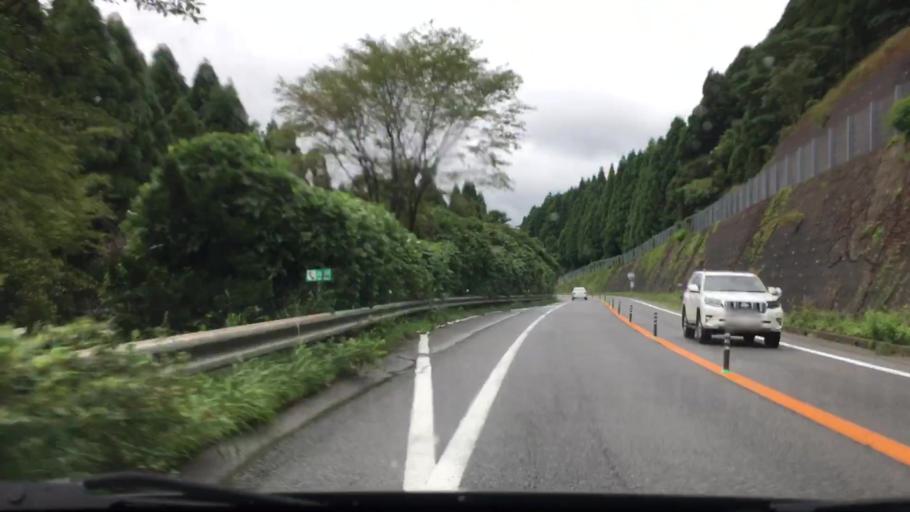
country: JP
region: Hyogo
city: Nishiwaki
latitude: 35.1270
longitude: 134.7879
